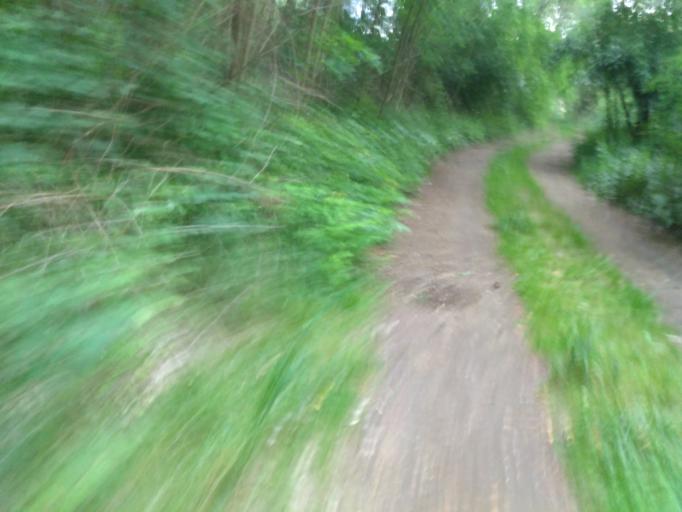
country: DE
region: Brandenburg
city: Elsterwerda
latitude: 51.4880
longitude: 13.5243
